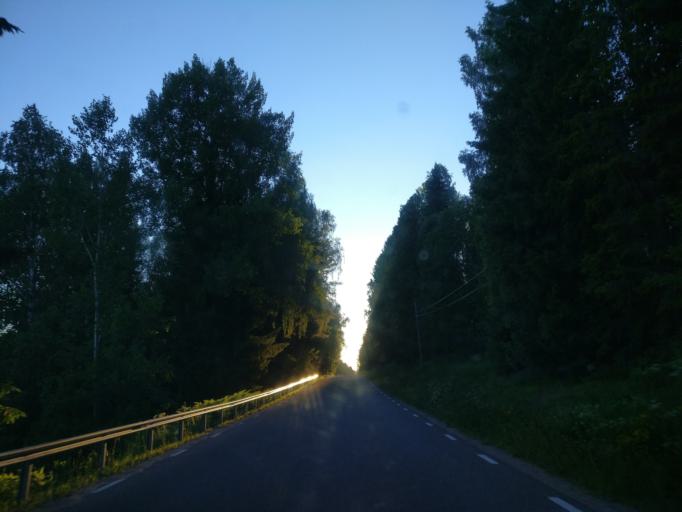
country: SE
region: Vaesternorrland
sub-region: Sundsvalls Kommun
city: Vi
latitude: 62.2473
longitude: 17.1113
